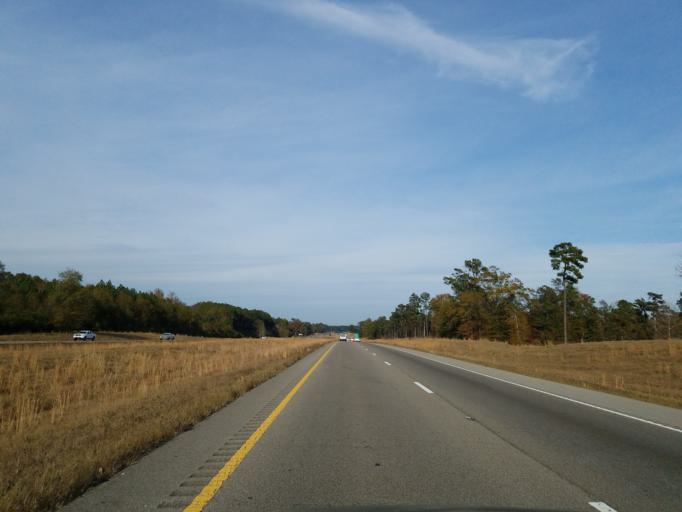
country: US
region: Mississippi
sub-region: Jones County
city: Ellisville
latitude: 31.5712
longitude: -89.2490
